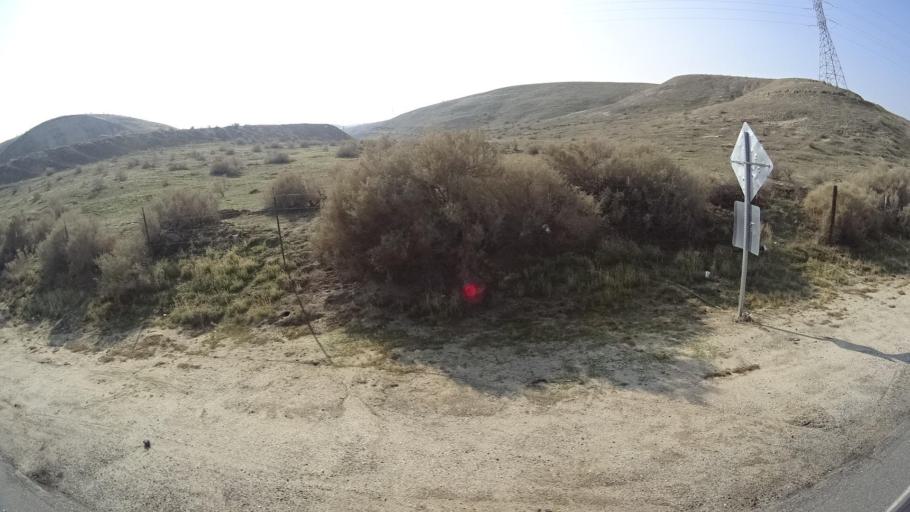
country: US
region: California
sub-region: Kern County
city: Ford City
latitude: 35.2841
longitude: -119.3305
